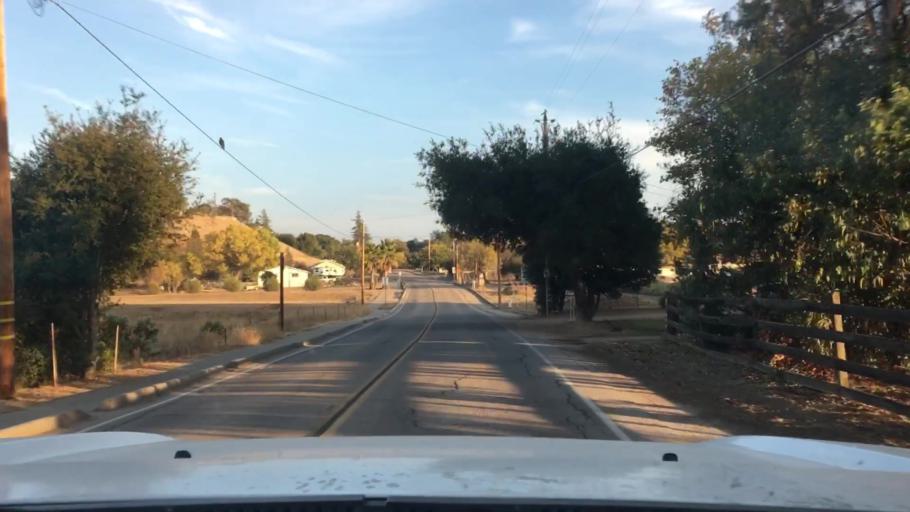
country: US
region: California
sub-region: San Luis Obispo County
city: Atascadero
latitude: 35.4602
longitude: -120.6712
